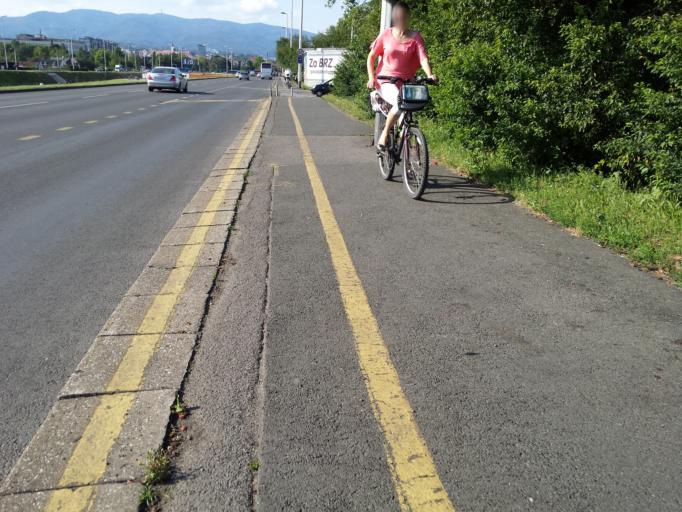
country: HR
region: Grad Zagreb
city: Novi Zagreb
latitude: 45.7960
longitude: 15.9797
